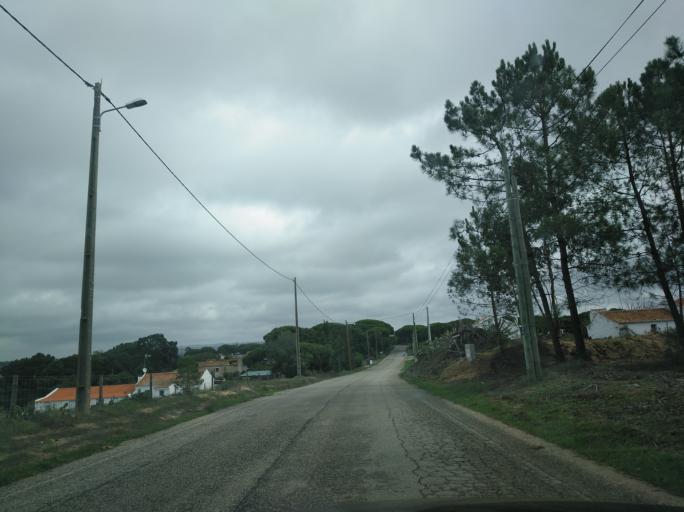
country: PT
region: Setubal
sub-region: Santiago do Cacem
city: Santo Andre
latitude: 38.1368
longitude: -8.7569
